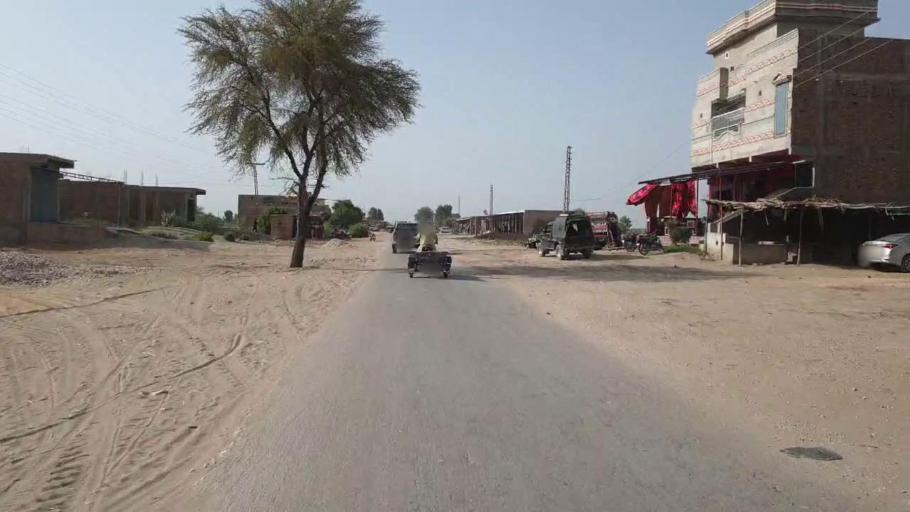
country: PK
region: Sindh
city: Sanghar
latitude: 26.2758
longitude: 68.9301
